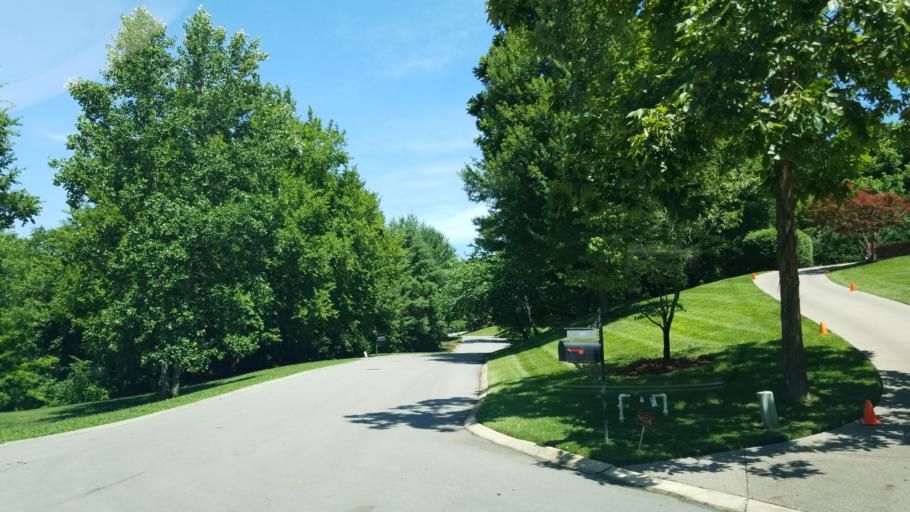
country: US
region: Tennessee
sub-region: Davidson County
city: Forest Hills
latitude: 36.0564
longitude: -86.8204
